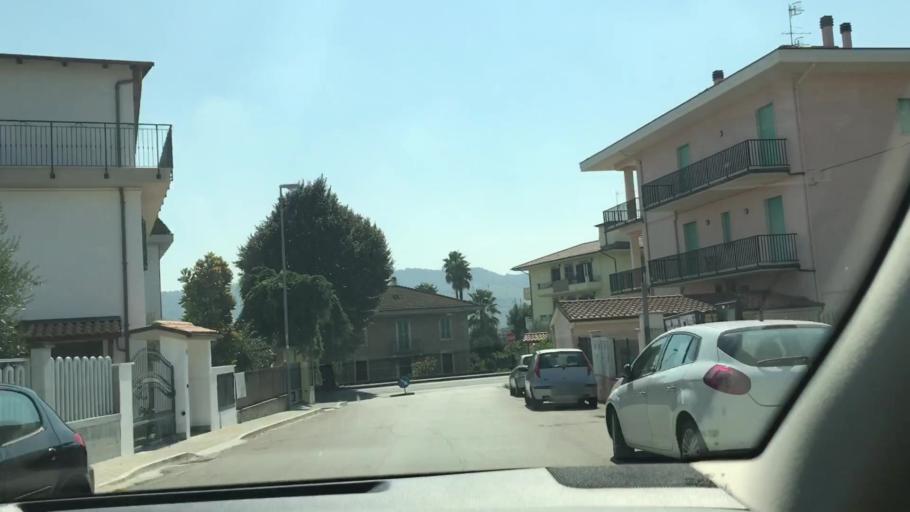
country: IT
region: The Marches
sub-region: Provincia di Ascoli Piceno
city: San Benedetto del Tronto
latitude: 42.9075
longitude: 13.8732
